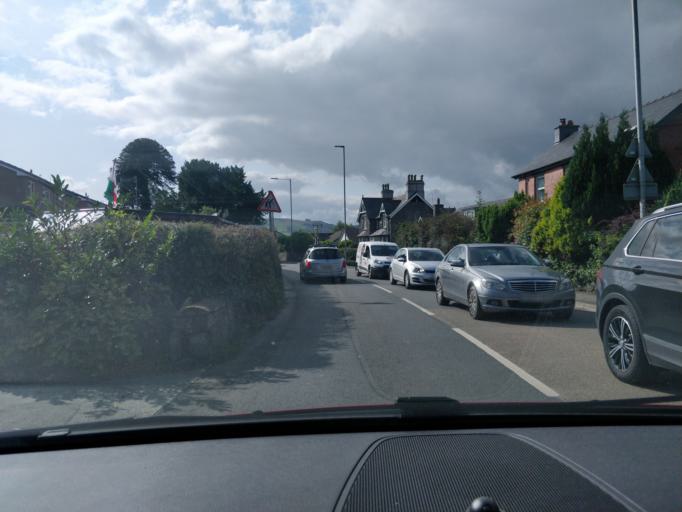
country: GB
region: Wales
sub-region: Conwy
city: Llanrwst
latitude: 53.1350
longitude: -3.7927
